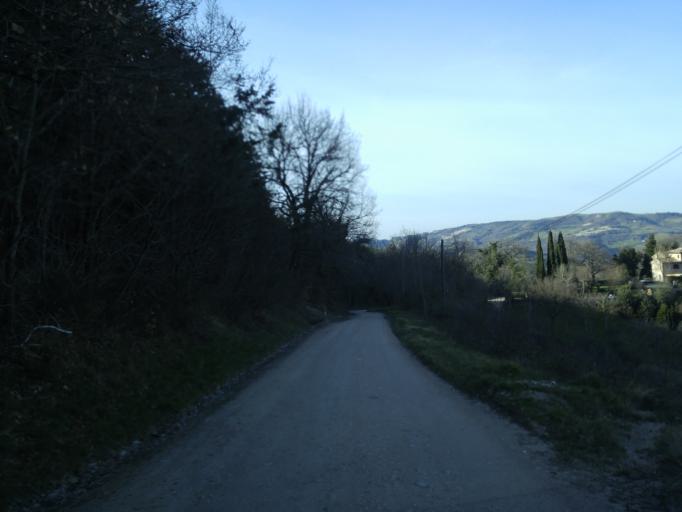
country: IT
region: The Marches
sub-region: Provincia di Pesaro e Urbino
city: Canavaccio
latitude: 43.6810
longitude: 12.6836
